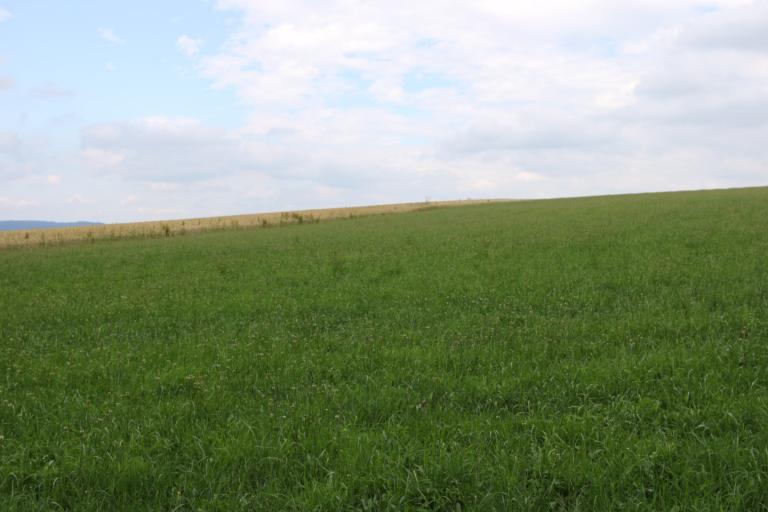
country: DE
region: Hesse
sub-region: Regierungsbezirk Darmstadt
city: Erbach
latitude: 49.6505
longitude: 8.9509
